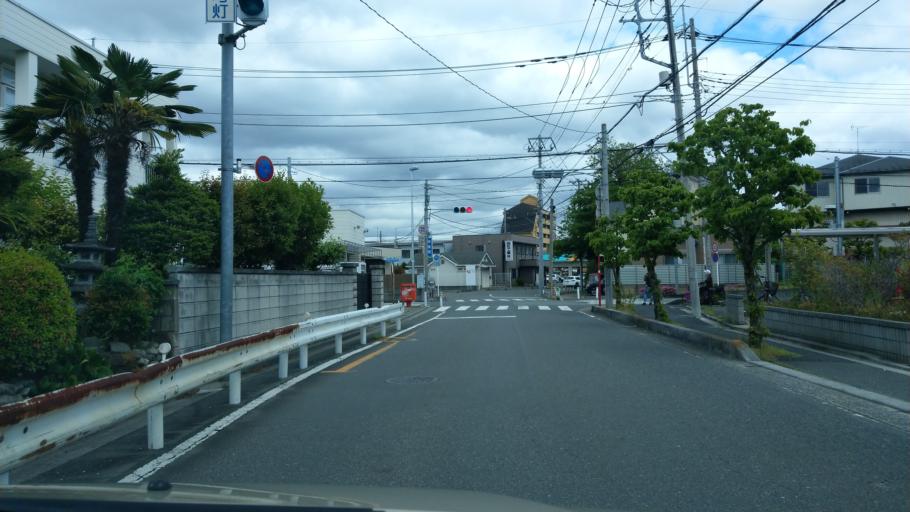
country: JP
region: Saitama
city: Yono
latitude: 35.8458
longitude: 139.6229
